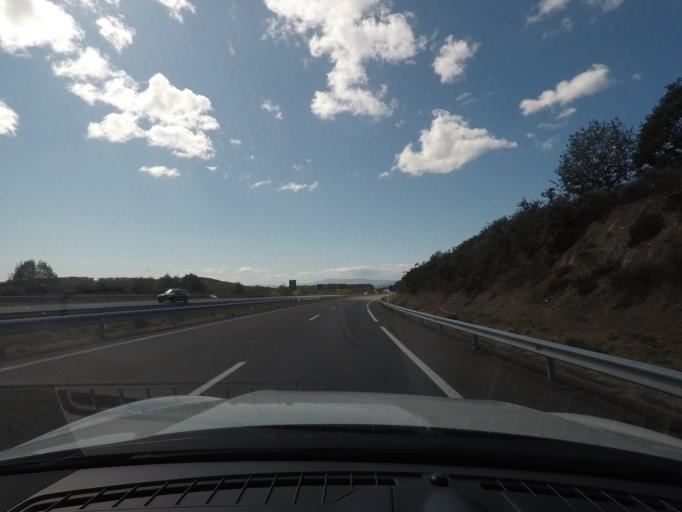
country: ES
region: Galicia
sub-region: Provincia de Ourense
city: Rios
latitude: 41.9517
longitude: -7.3323
